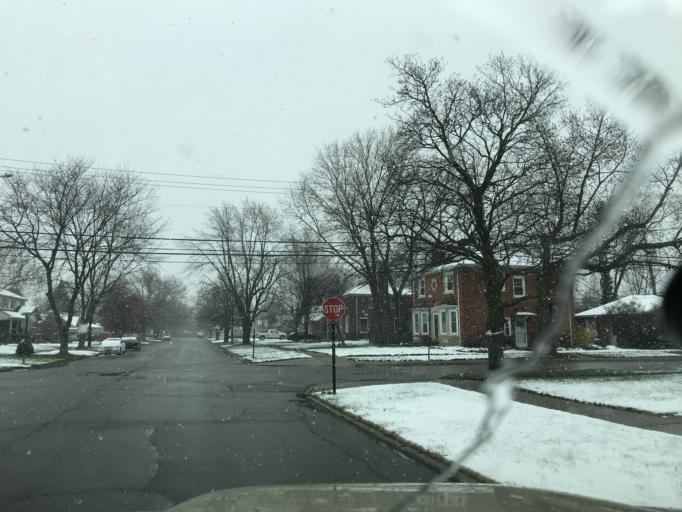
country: US
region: Michigan
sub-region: Wayne County
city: Allen Park
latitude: 42.2374
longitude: -83.2188
